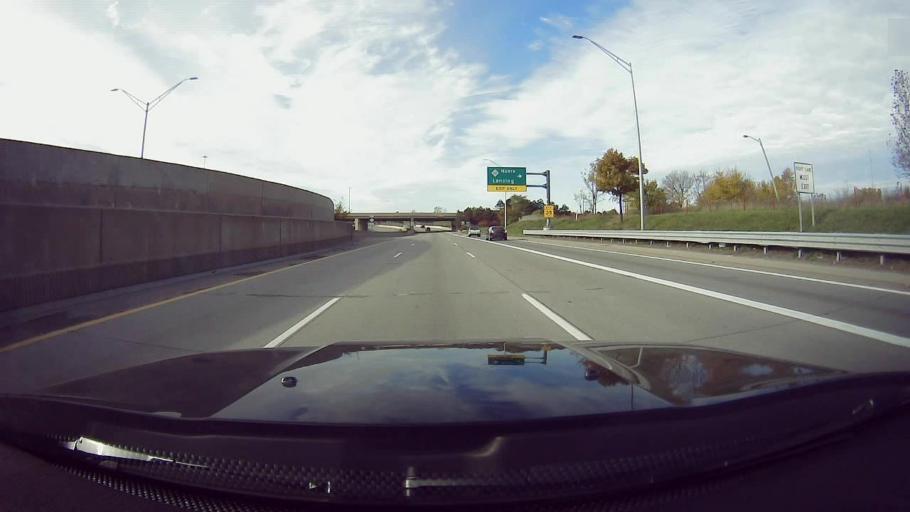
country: US
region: Michigan
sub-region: Wayne County
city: Highland Park
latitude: 42.3993
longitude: -83.1079
